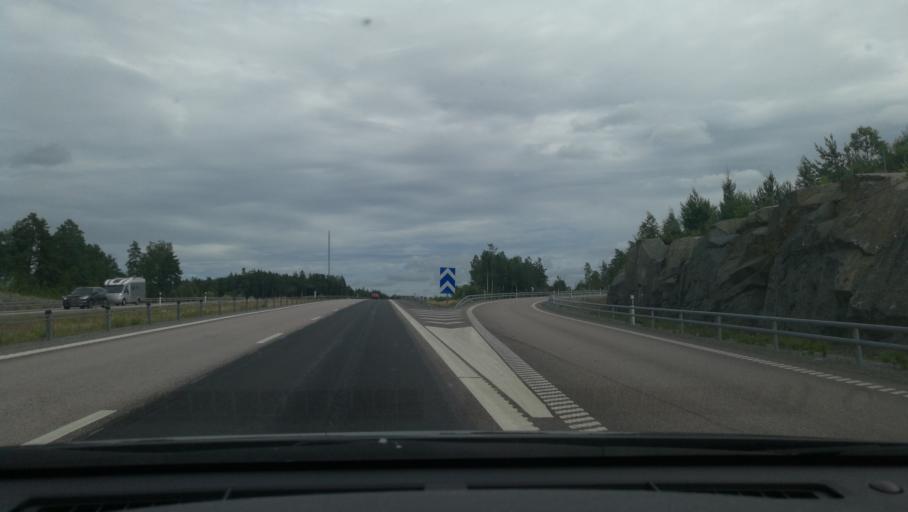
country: SE
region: Uppsala
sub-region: Enkopings Kommun
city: Hummelsta
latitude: 59.6386
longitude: 16.8789
